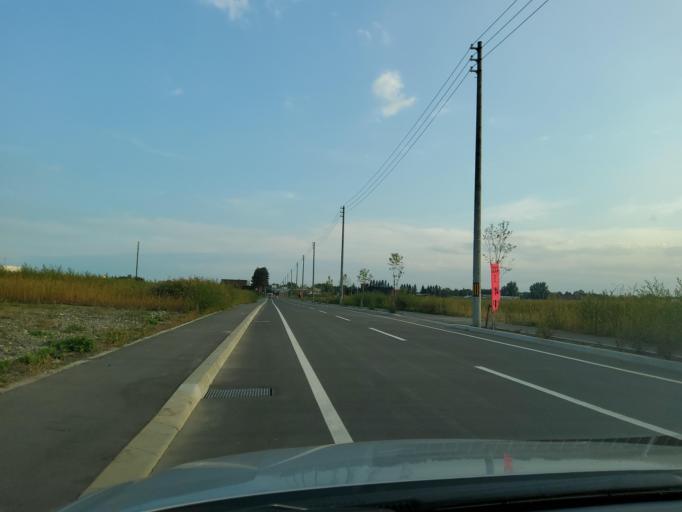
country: JP
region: Hokkaido
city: Obihiro
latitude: 42.9381
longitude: 143.1531
